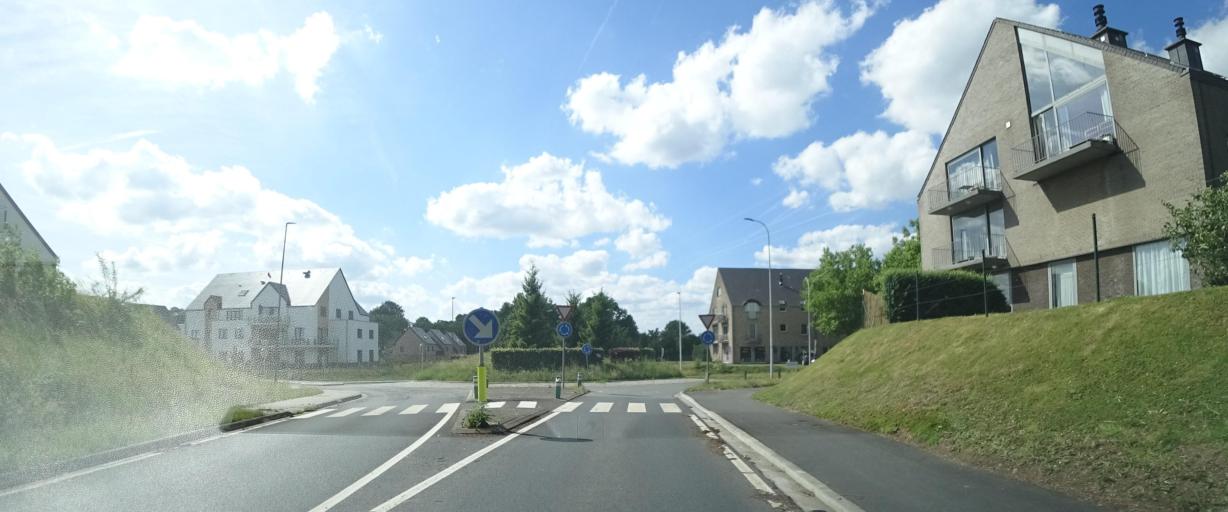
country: BE
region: Wallonia
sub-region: Province du Brabant Wallon
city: Wavre
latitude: 50.7052
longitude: 4.6298
